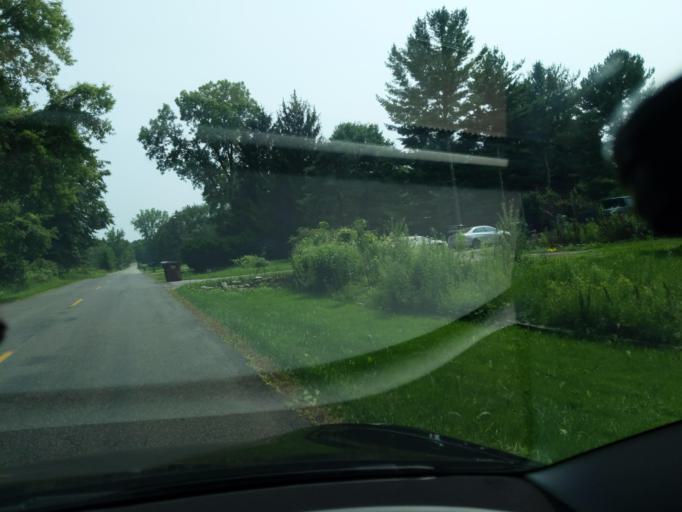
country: US
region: Michigan
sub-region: Ingham County
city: Holt
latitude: 42.6358
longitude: -84.5579
